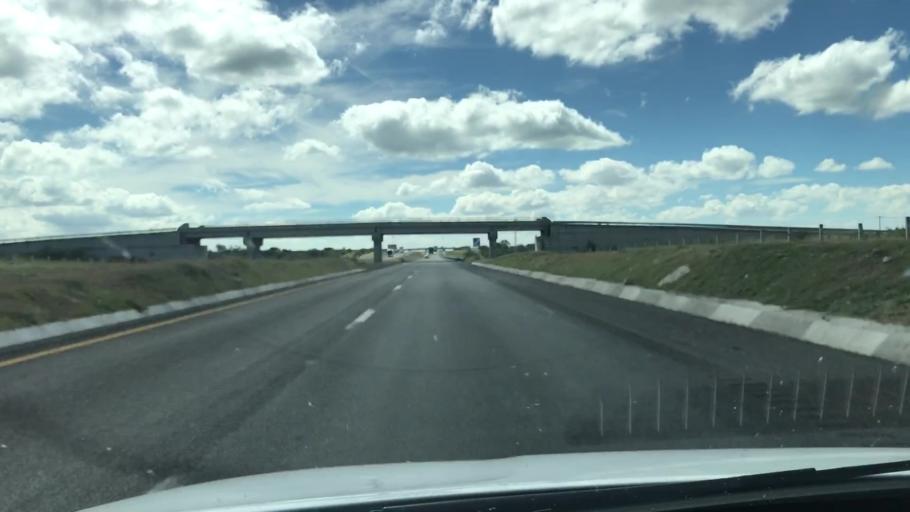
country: MX
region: Guanajuato
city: San Jose Temascatio
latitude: 20.7260
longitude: -101.2879
